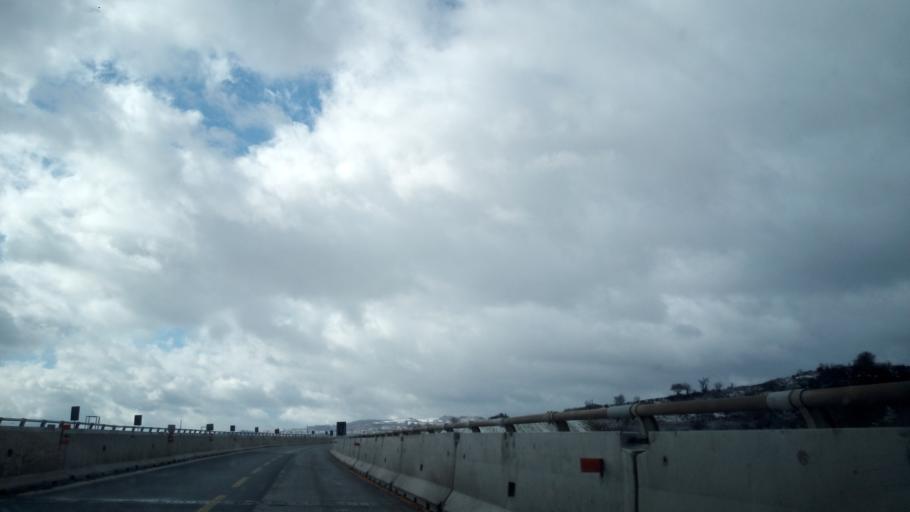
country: IT
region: Campania
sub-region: Provincia di Avellino
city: Scampitella
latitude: 41.0630
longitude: 15.3098
